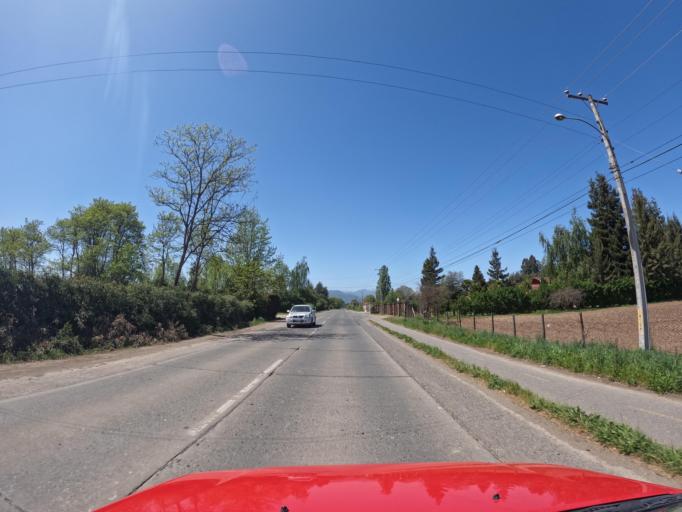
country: CL
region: Maule
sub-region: Provincia de Linares
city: Linares
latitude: -35.8294
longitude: -71.5055
